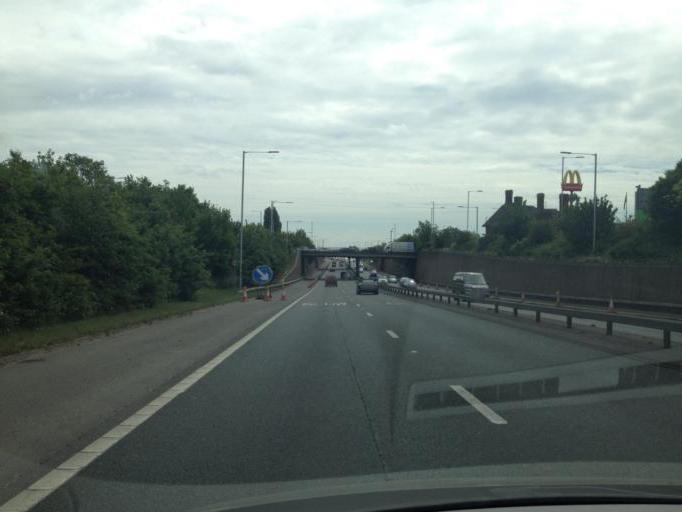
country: GB
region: England
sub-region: Greater London
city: Northolt
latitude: 51.5439
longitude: -0.3805
